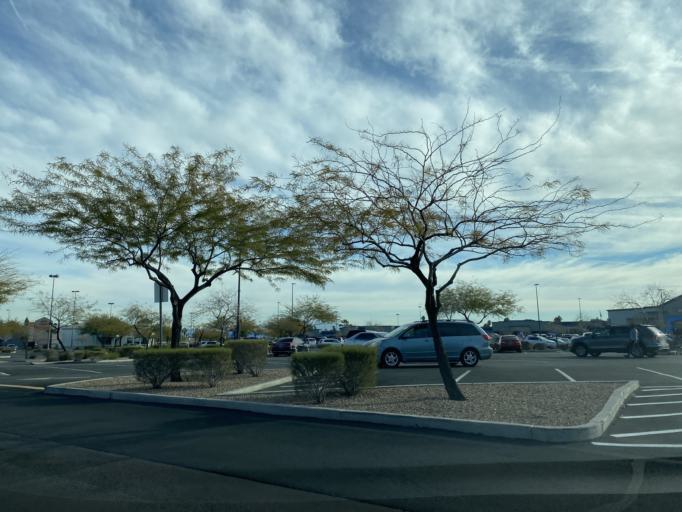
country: US
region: Nevada
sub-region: Clark County
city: Spring Valley
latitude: 36.1249
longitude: -115.2458
